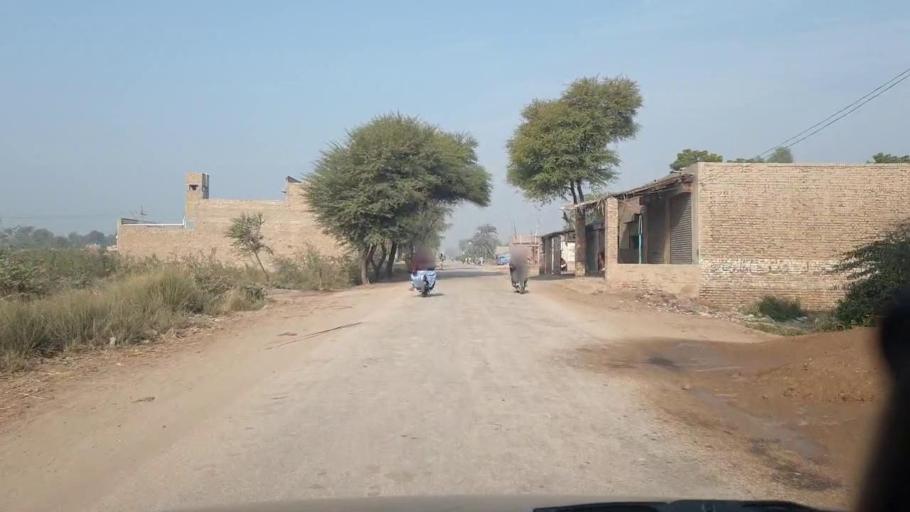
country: PK
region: Sindh
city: Shahdadpur
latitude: 25.9313
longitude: 68.6128
